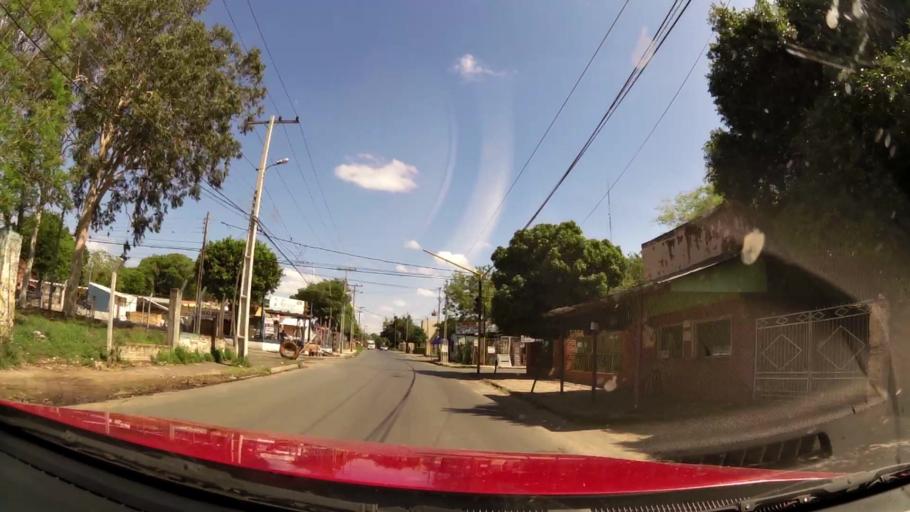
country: PY
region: Central
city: Colonia Mariano Roque Alonso
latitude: -25.2511
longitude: -57.5534
